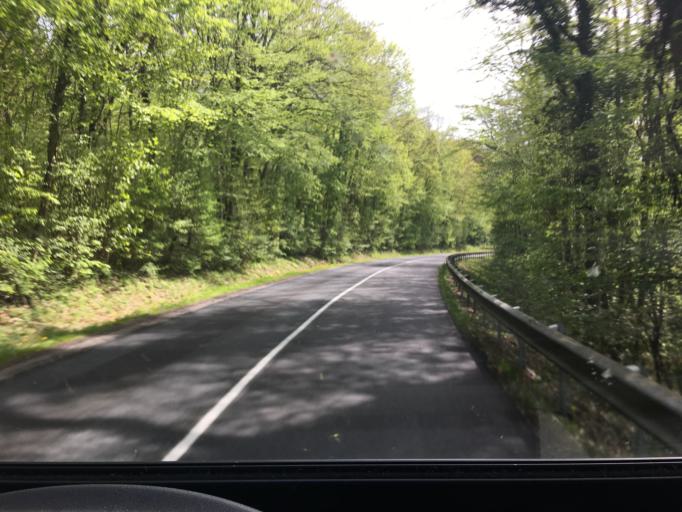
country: FR
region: Lorraine
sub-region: Departement de Meurthe-et-Moselle
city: Velaine-en-Haye
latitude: 48.6643
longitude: 6.0148
